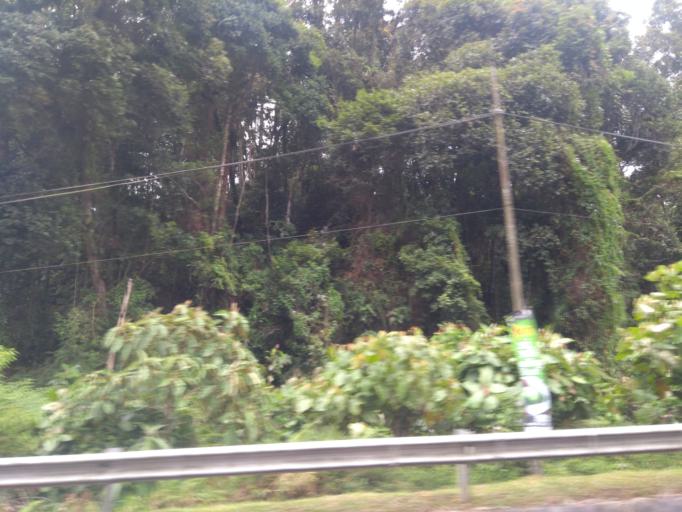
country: MY
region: Pahang
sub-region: Cameron Highlands
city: Tanah Rata
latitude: 4.4687
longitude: 101.3699
